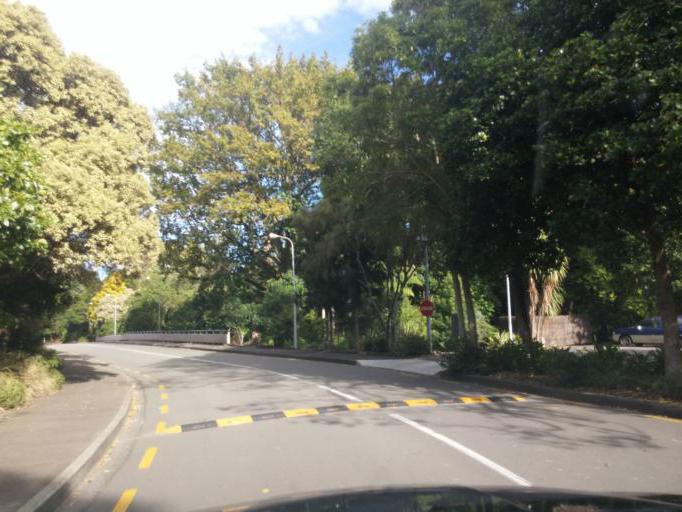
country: NZ
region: Manawatu-Wanganui
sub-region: Palmerston North City
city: Palmerston North
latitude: -40.3849
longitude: 175.6156
